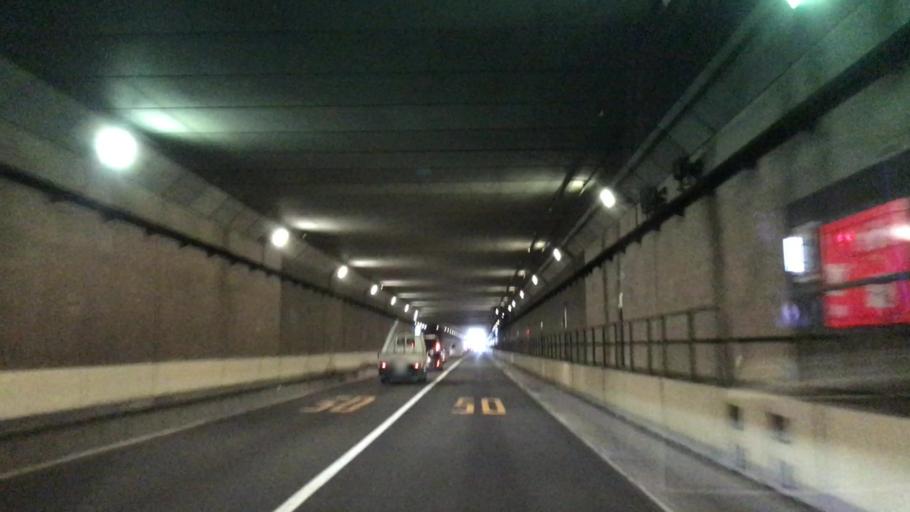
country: JP
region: Hokkaido
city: Sapporo
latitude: 43.0592
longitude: 141.3576
